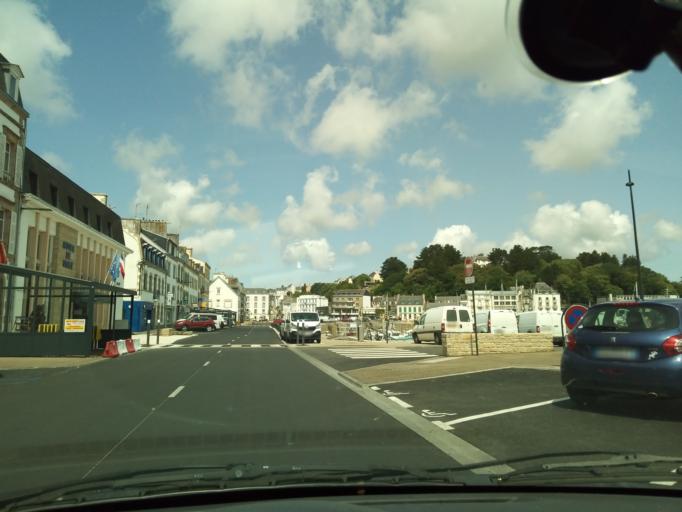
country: FR
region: Brittany
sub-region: Departement du Finistere
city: Audierne
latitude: 48.0213
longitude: -4.5374
